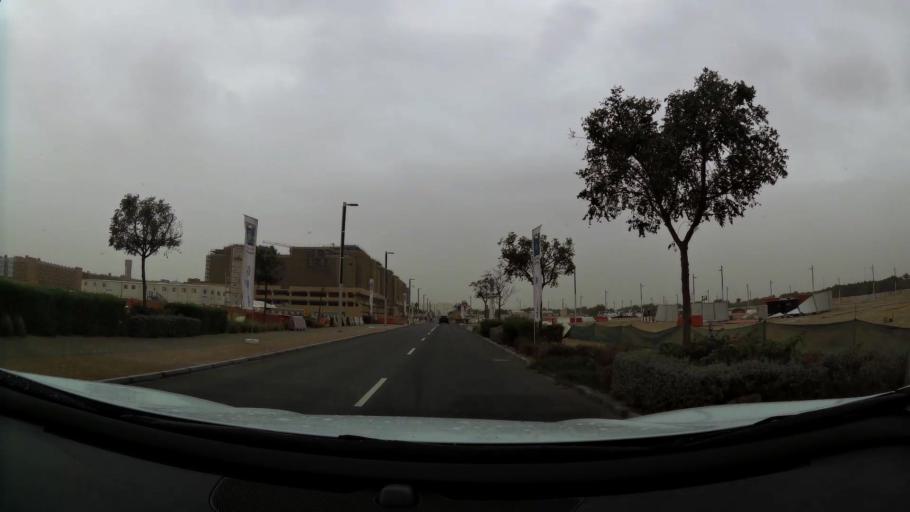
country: AE
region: Abu Dhabi
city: Abu Dhabi
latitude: 24.4343
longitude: 54.6233
